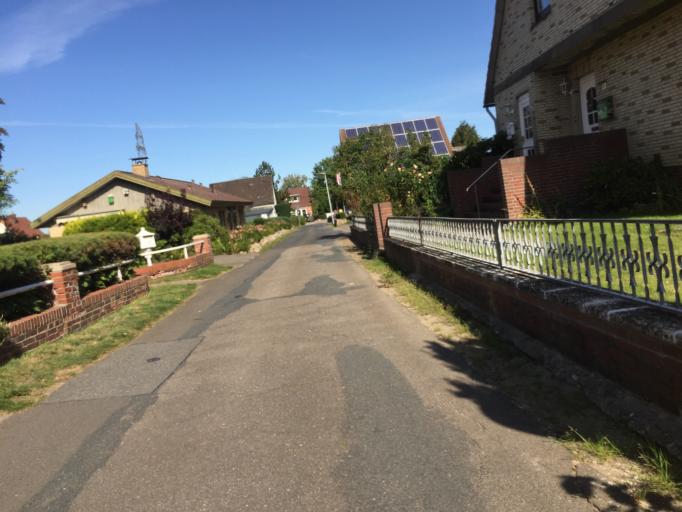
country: DE
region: Schleswig-Holstein
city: Itzehoe
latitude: 53.9103
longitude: 9.4951
